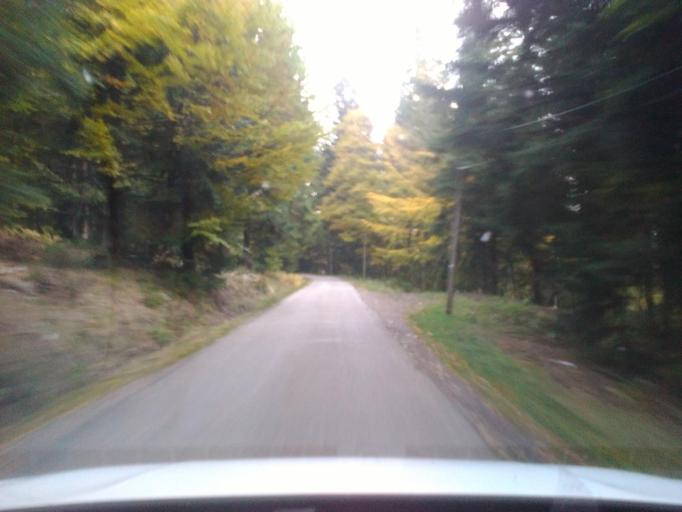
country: FR
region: Lorraine
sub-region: Departement des Vosges
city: Le Tholy
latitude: 48.0883
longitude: 6.7813
